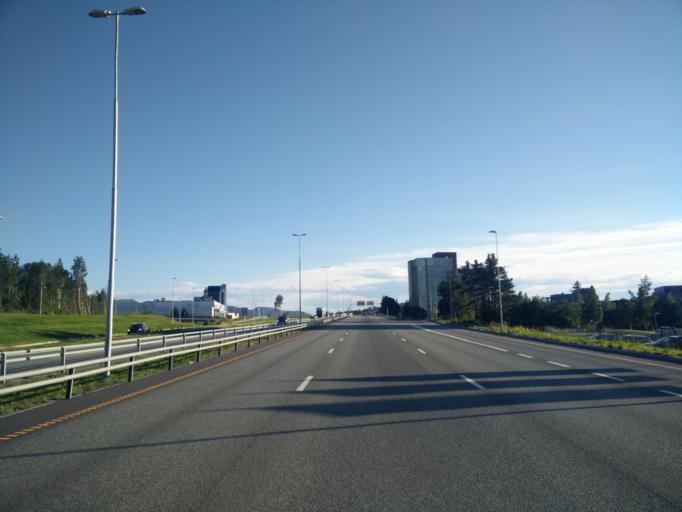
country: NO
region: Sor-Trondelag
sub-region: Trondheim
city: Trondheim
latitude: 63.3655
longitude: 10.3768
